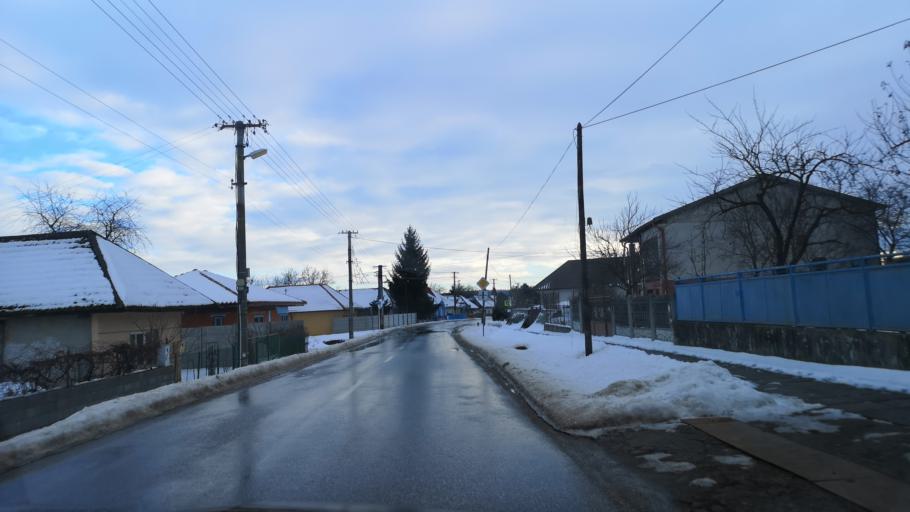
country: SK
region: Nitriansky
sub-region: Okres Nitra
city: Vrable
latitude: 48.1337
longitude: 18.3358
